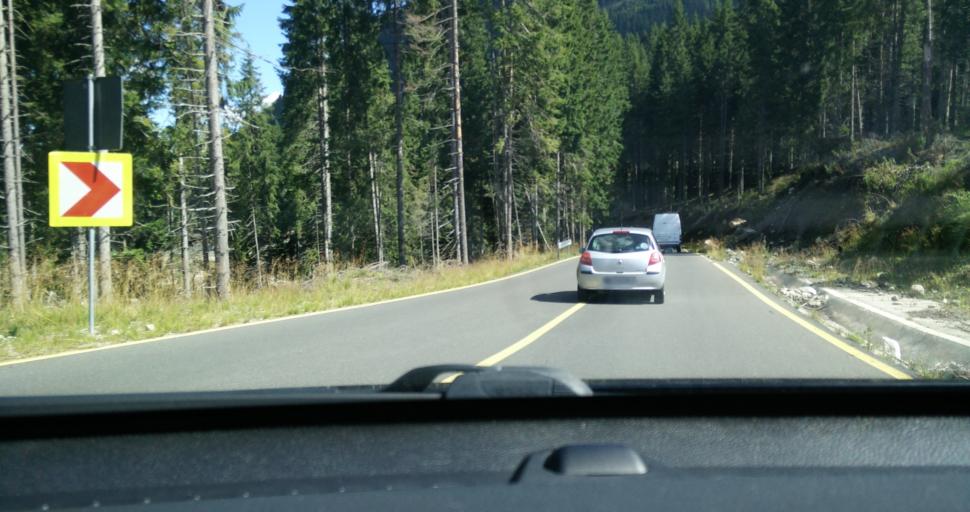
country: RO
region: Gorj
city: Novaci-Straini
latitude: 45.3914
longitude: 23.6320
